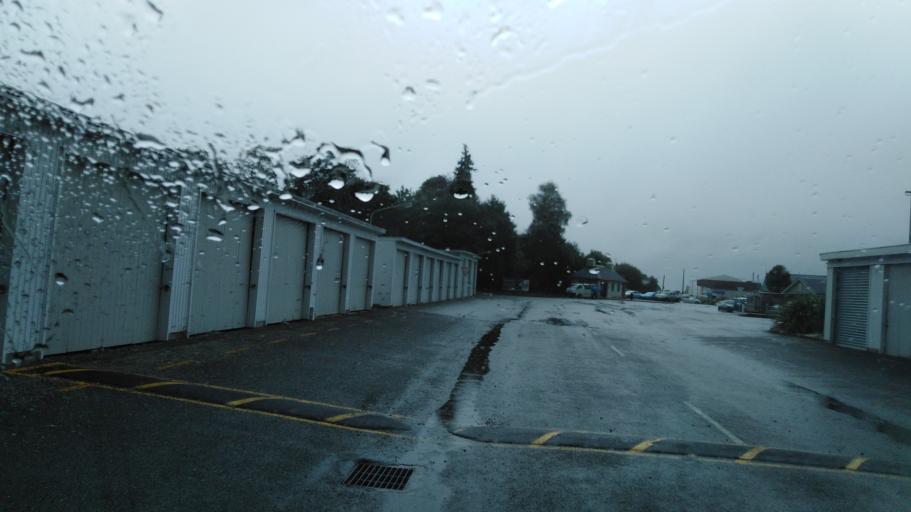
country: NZ
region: Marlborough
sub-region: Marlborough District
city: Picton
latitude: -41.2770
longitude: 173.7686
